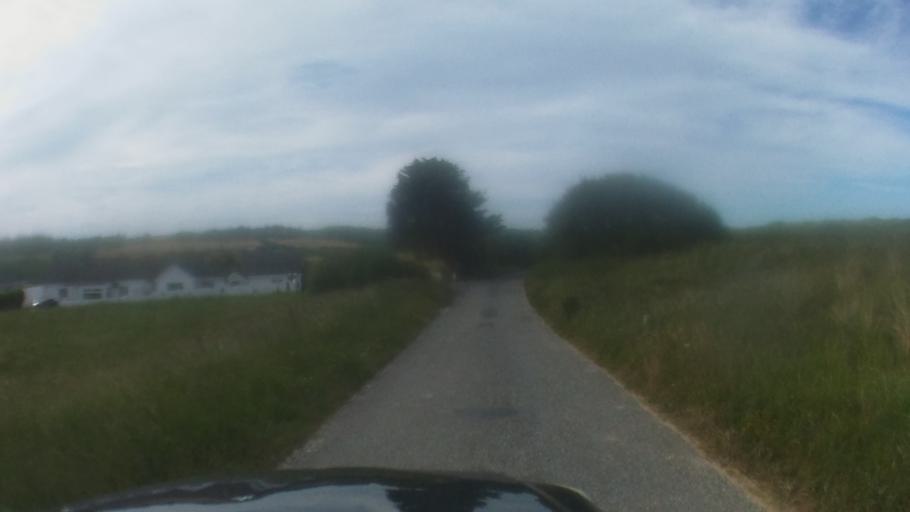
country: IE
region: Leinster
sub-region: Loch Garman
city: Castlebridge
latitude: 52.3908
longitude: -6.3639
